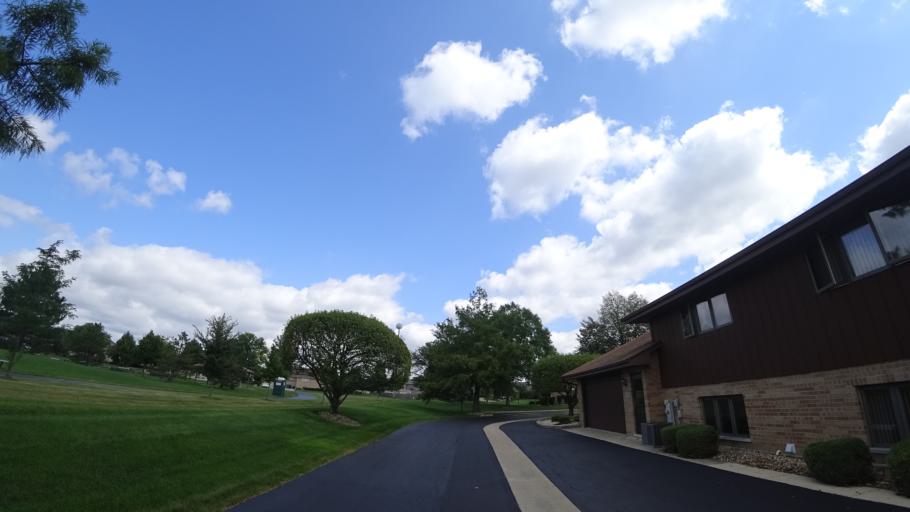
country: US
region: Illinois
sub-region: Will County
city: Mokena
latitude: 41.5596
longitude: -87.8788
